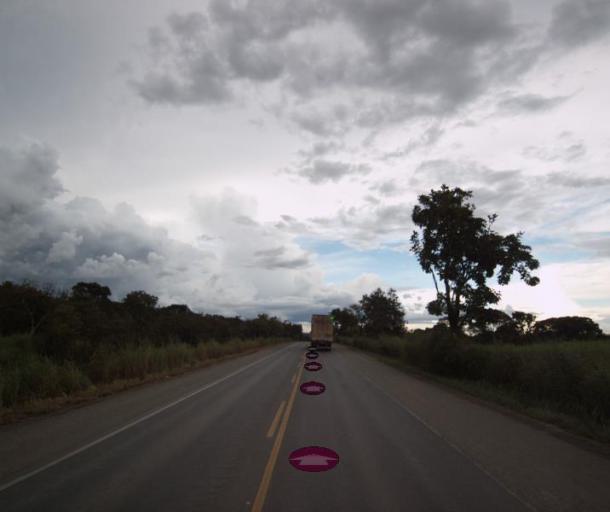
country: BR
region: Goias
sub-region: Itapaci
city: Itapaci
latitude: -14.9509
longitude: -49.3775
